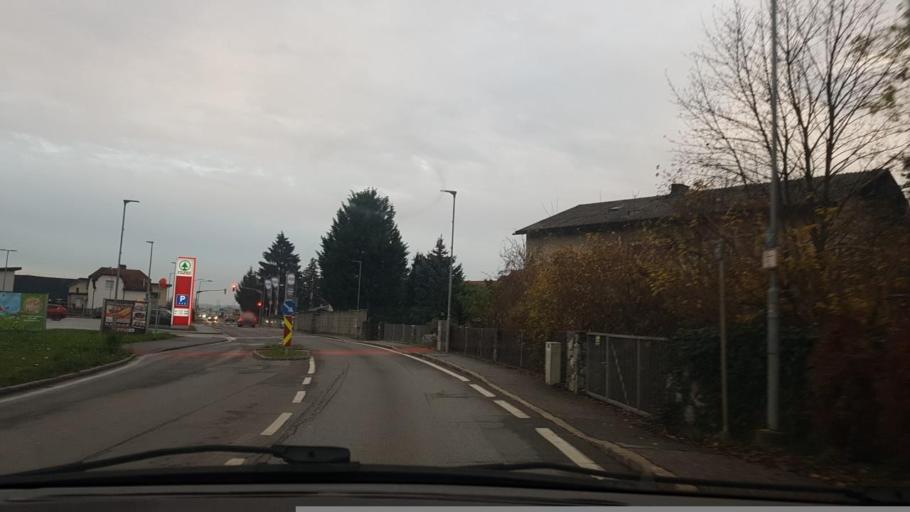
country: AT
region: Styria
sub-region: Politischer Bezirk Graz-Umgebung
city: Feldkirchen bei Graz
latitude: 47.0131
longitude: 15.4288
